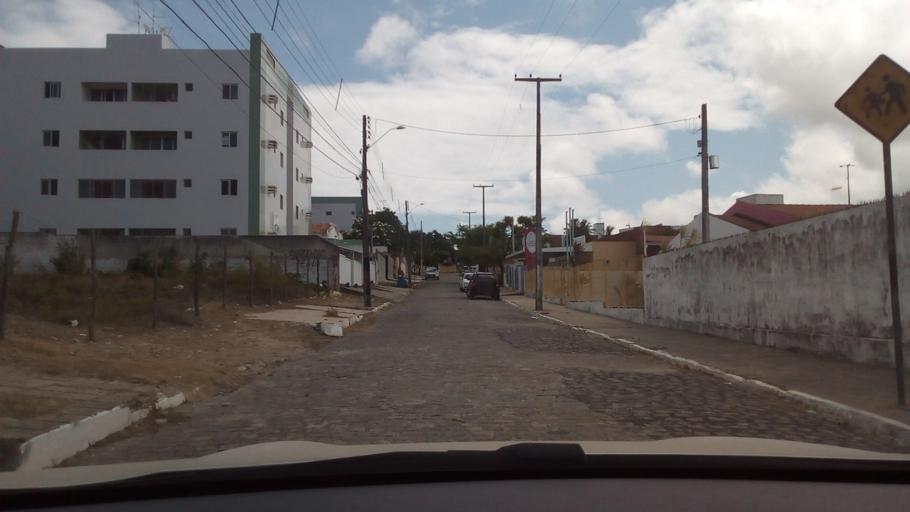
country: BR
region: Paraiba
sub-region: Joao Pessoa
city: Joao Pessoa
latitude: -7.1457
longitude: -34.8315
